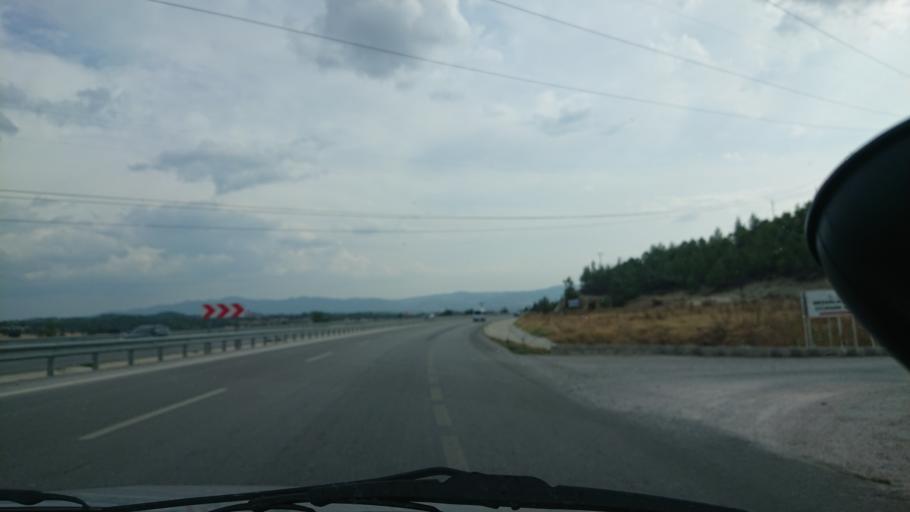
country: TR
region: Kuetahya
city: Gediz
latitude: 39.0280
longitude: 29.4163
